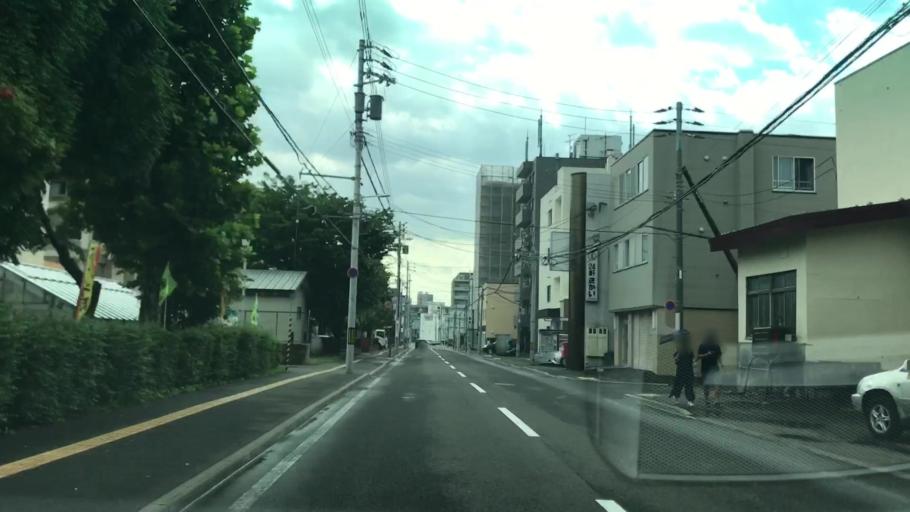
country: JP
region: Hokkaido
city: Sapporo
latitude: 43.0727
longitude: 141.3129
